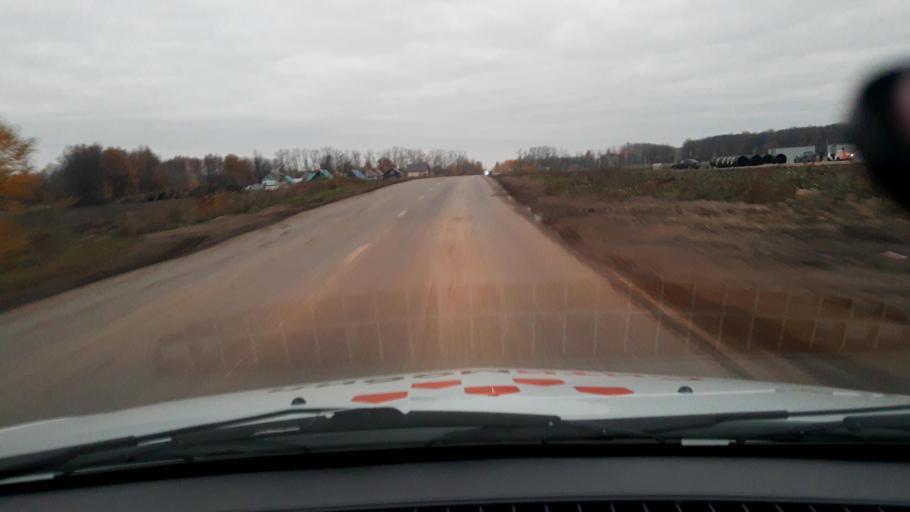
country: RU
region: Bashkortostan
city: Kabakovo
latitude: 54.6960
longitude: 56.1491
